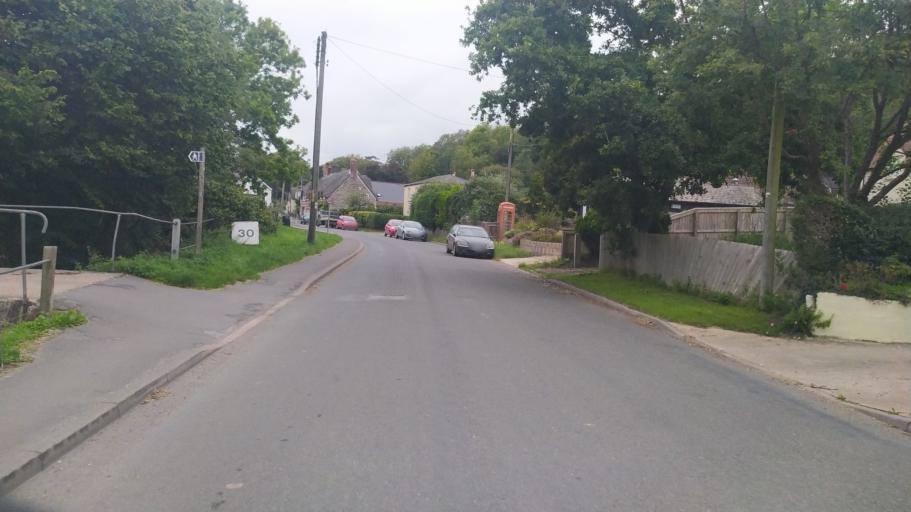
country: GB
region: England
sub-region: Dorset
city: Dorchester
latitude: 50.7958
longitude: -2.4185
